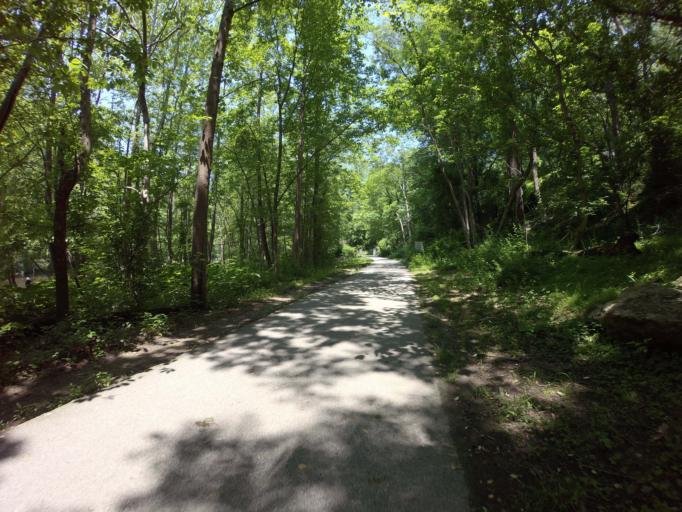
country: US
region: Maryland
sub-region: Howard County
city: Ilchester
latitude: 39.2448
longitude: -76.7519
